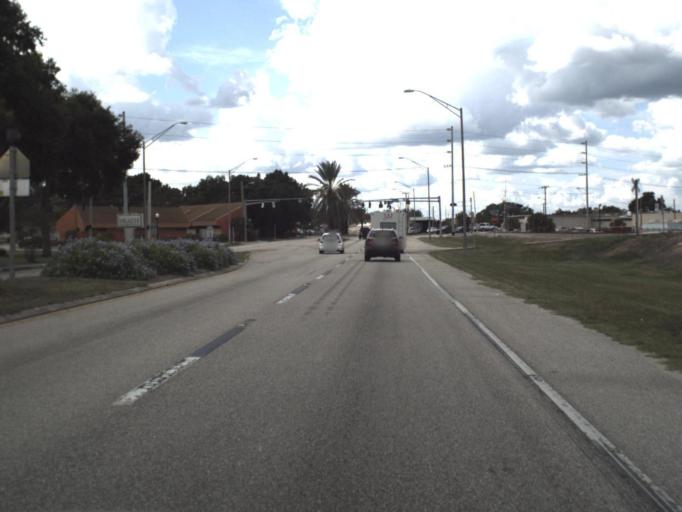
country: US
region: Florida
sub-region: Polk County
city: Lakeland
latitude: 28.0412
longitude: -81.9436
